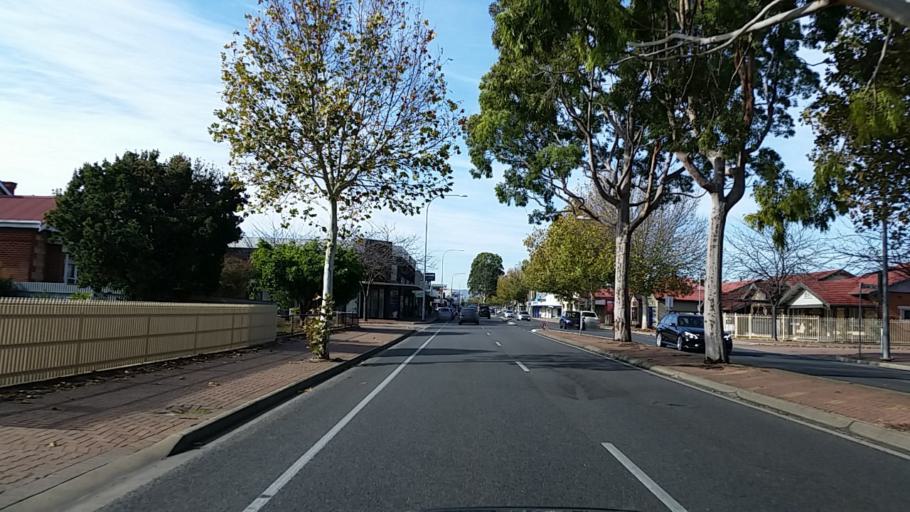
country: AU
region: South Australia
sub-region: City of West Torrens
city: Thebarton
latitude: -34.9243
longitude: 138.5568
